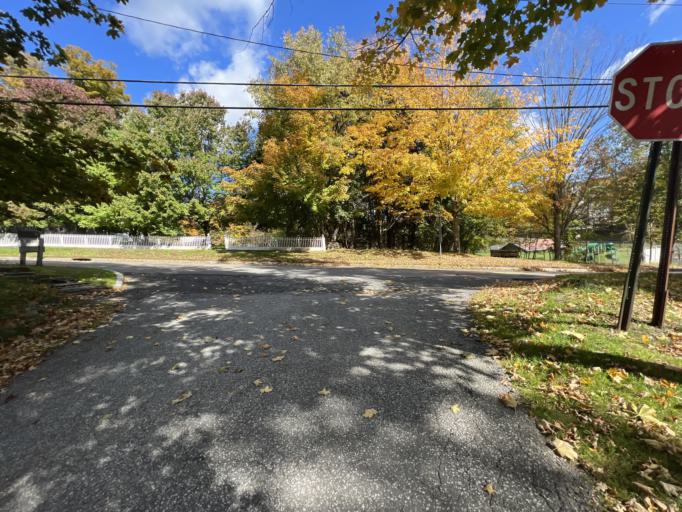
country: US
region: New York
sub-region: Albany County
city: Altamont
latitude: 42.5152
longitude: -74.1348
